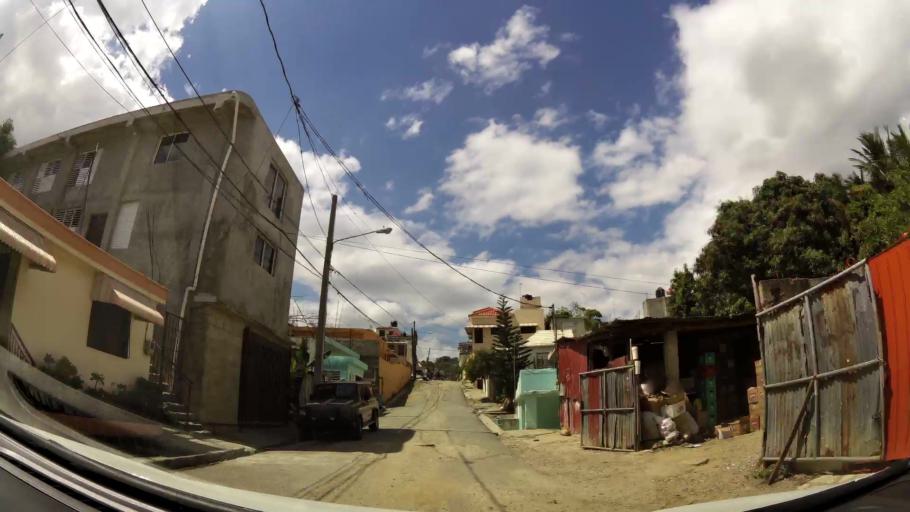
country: DO
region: San Cristobal
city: San Cristobal
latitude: 18.4080
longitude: -70.1152
